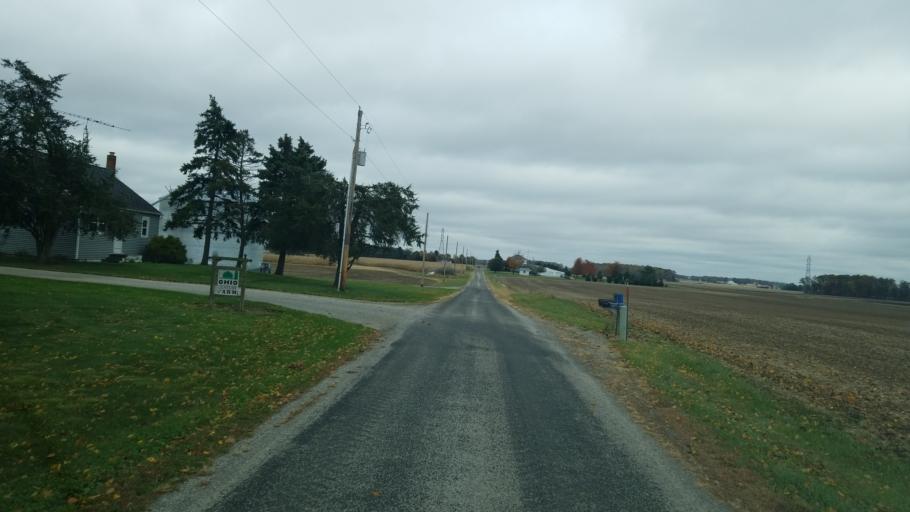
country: US
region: Ohio
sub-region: Crawford County
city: Bucyrus
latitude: 40.9201
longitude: -82.8463
